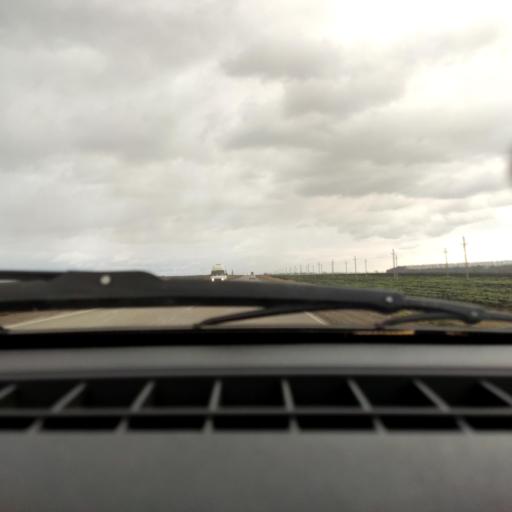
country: RU
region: Bashkortostan
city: Iglino
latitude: 54.7590
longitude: 56.2750
